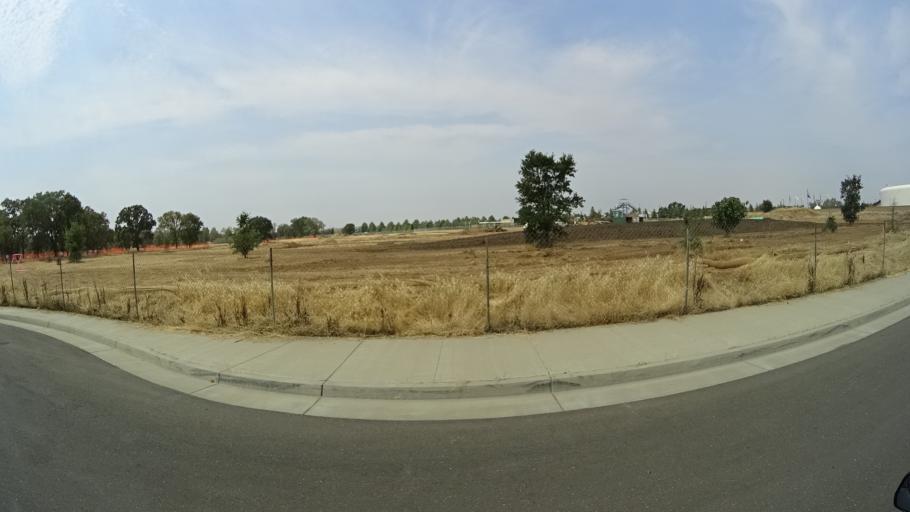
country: US
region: California
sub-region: Sacramento County
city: Elk Grove
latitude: 38.4044
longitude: -121.3991
